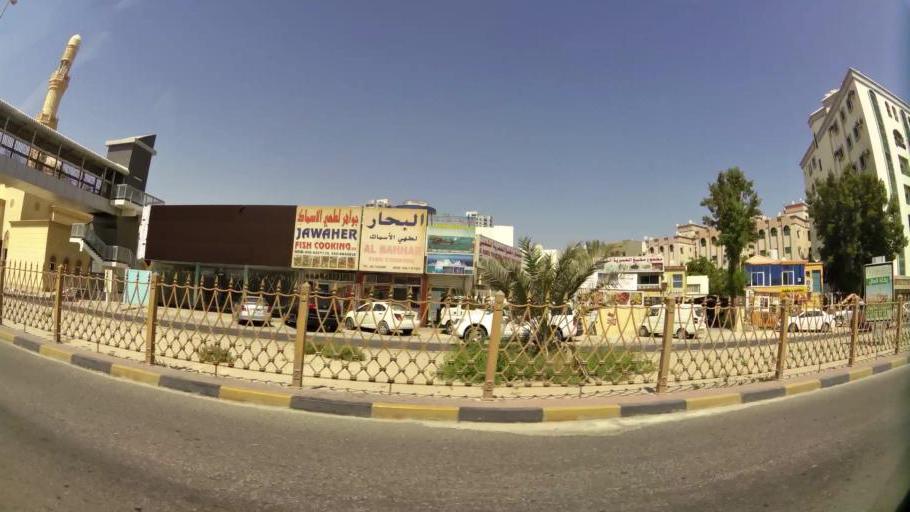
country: AE
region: Ajman
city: Ajman
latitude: 25.4005
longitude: 55.4530
